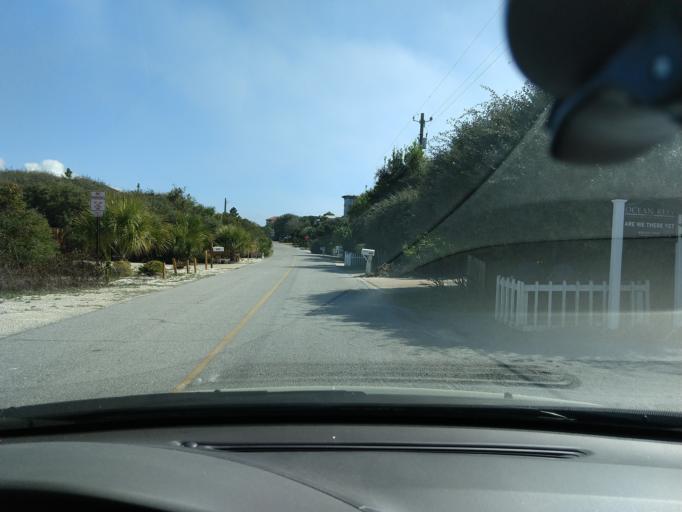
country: US
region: Florida
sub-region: Walton County
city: Seaside
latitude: 30.3366
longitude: -86.1952
